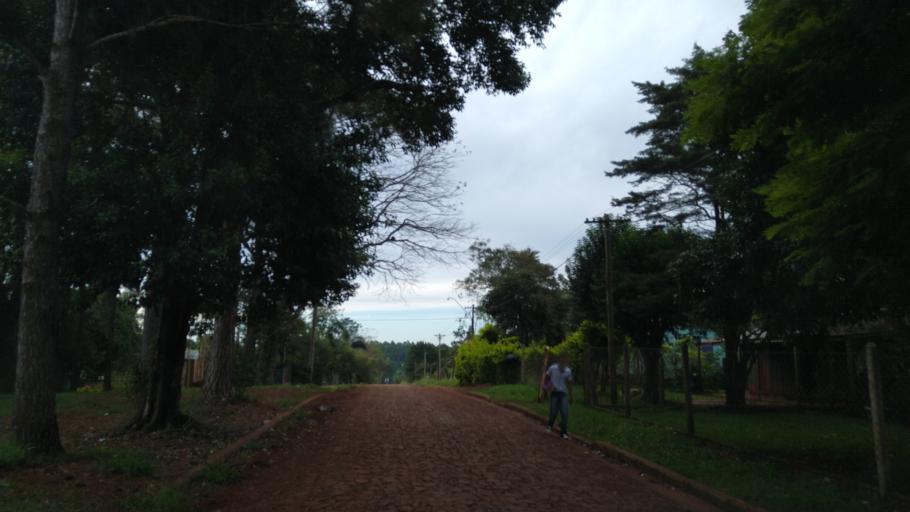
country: AR
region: Misiones
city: Capiovi
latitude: -26.9439
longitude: -55.0956
